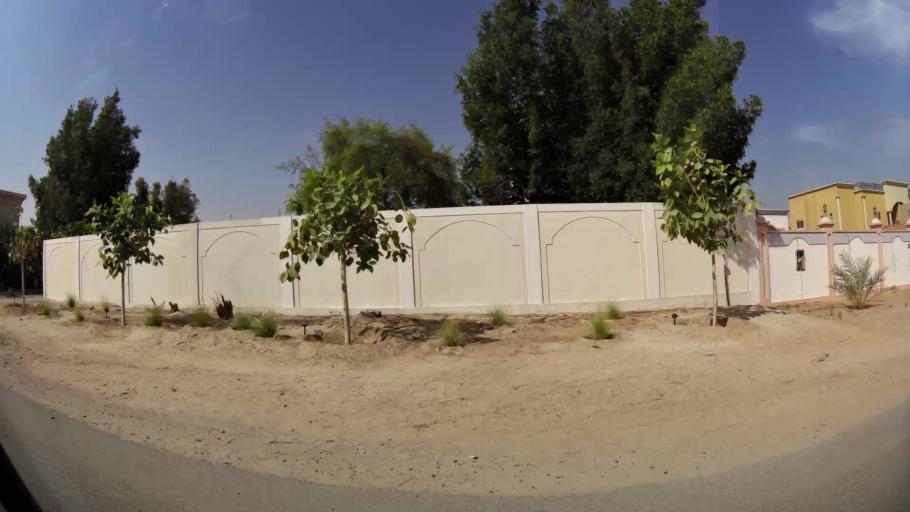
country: AE
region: Ash Shariqah
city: Sharjah
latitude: 25.2684
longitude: 55.4103
